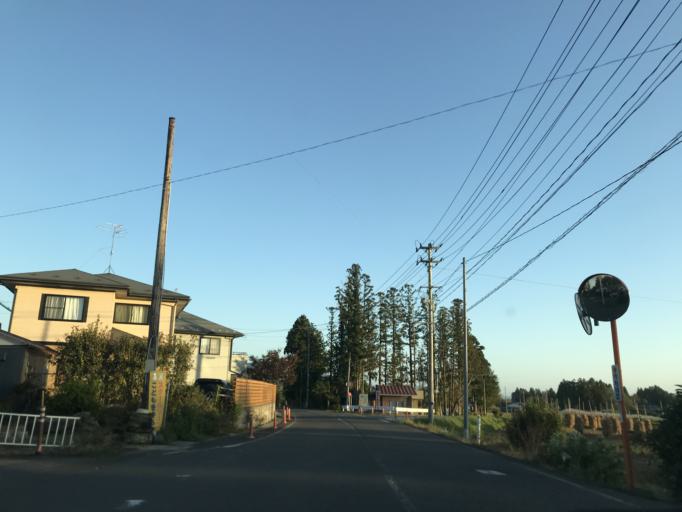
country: JP
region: Iwate
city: Mizusawa
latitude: 39.0586
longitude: 141.1105
